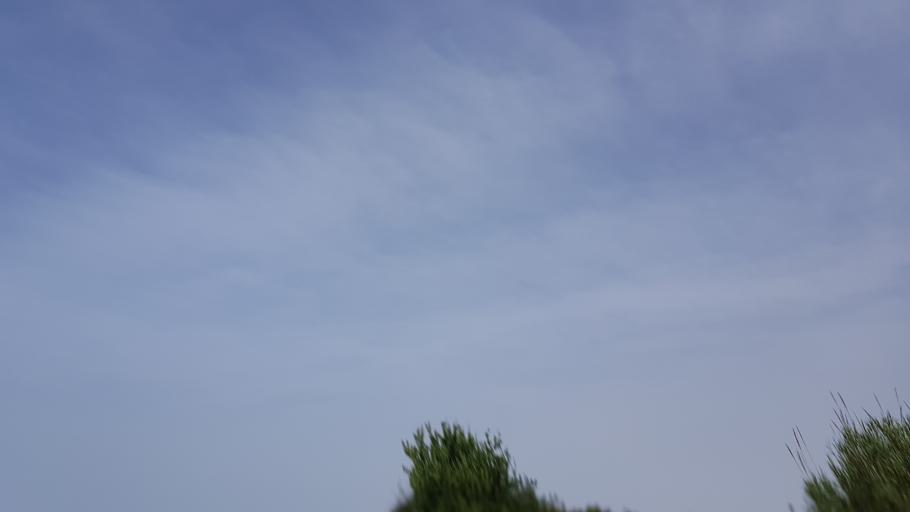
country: IT
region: Apulia
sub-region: Provincia di Brindisi
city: La Rosa
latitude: 40.5918
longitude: 17.9982
